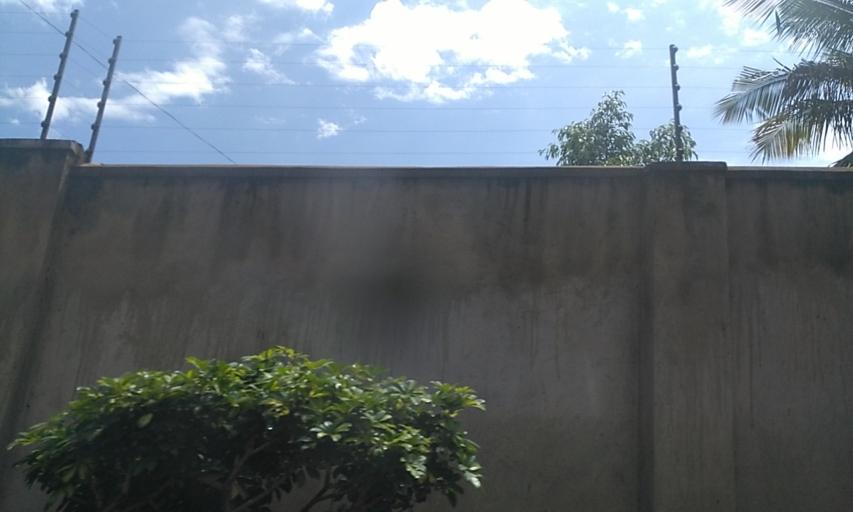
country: UG
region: Central Region
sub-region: Kampala District
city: Kampala
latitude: 0.3328
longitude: 32.5987
